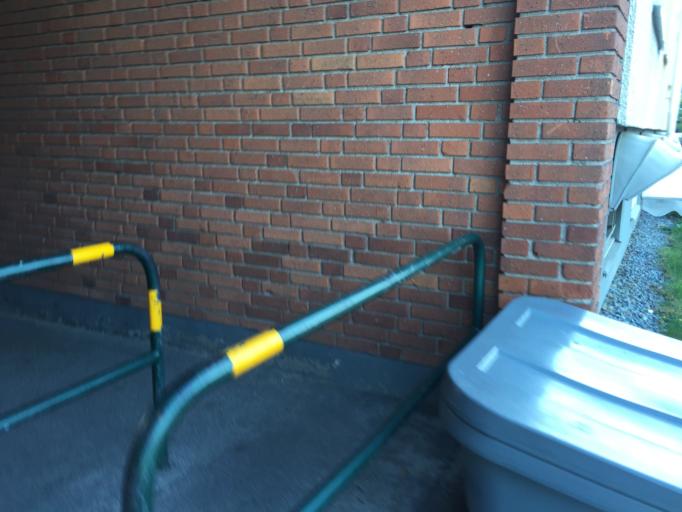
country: SE
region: Stockholm
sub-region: Taby Kommun
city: Taby
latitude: 59.4475
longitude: 18.0828
